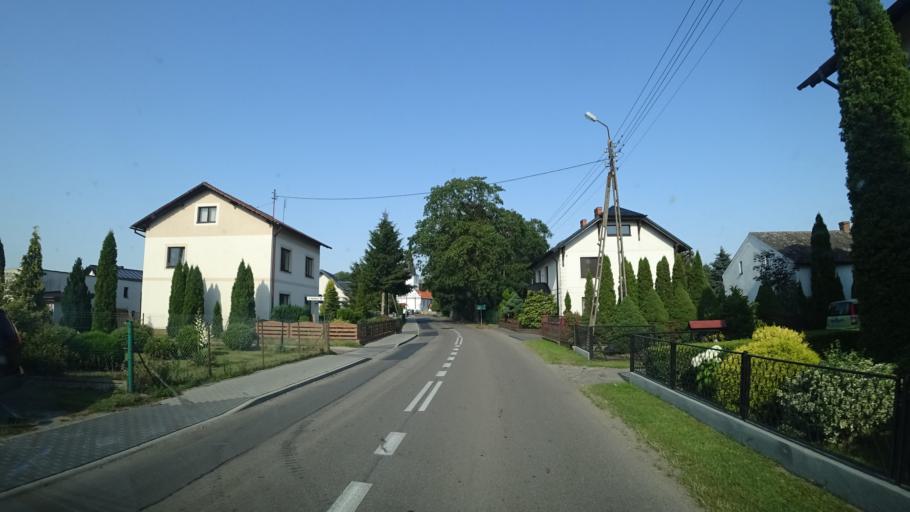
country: PL
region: Pomeranian Voivodeship
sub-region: Powiat czluchowski
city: Przechlewo
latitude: 53.8223
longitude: 17.3744
